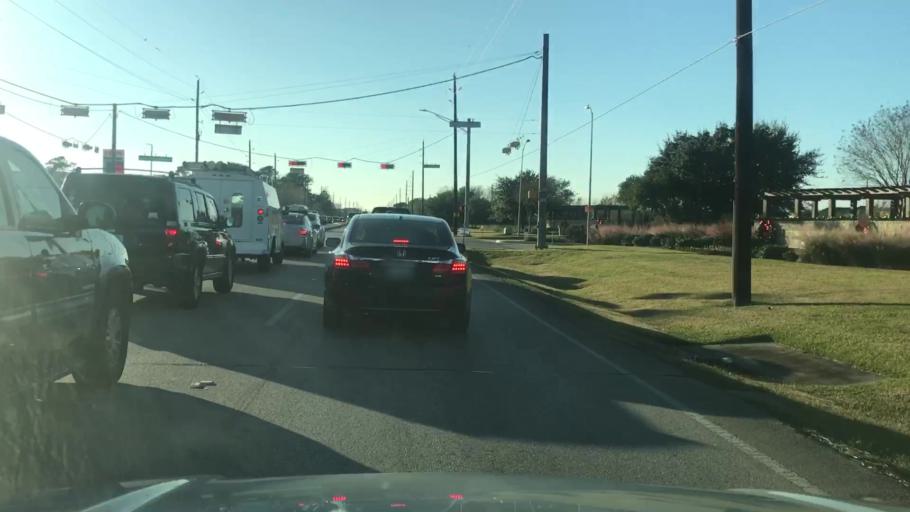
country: US
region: Texas
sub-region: Harris County
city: Katy
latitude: 29.8318
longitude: -95.7452
